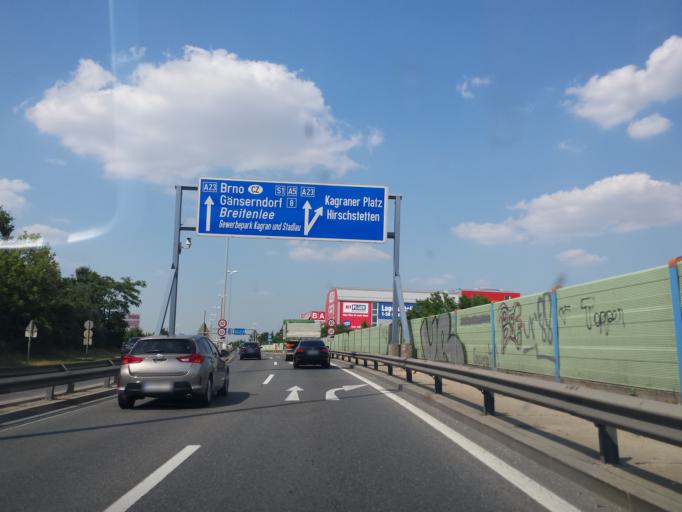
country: AT
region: Lower Austria
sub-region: Politischer Bezirk Wien-Umgebung
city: Gerasdorf bei Wien
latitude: 48.2359
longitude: 16.4571
